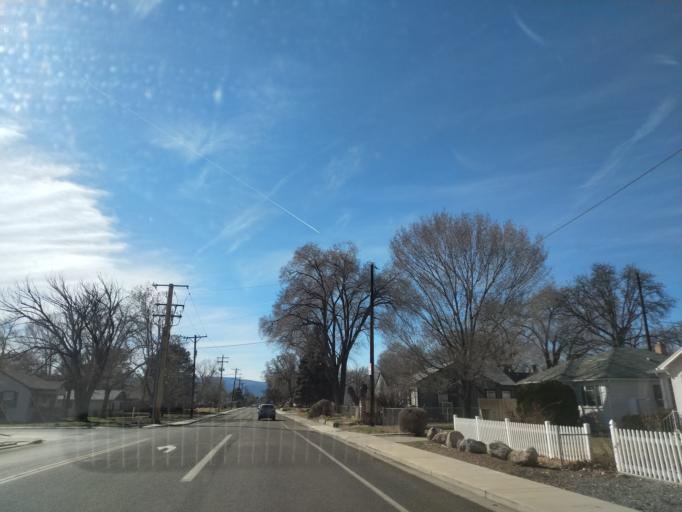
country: US
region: Colorado
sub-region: Mesa County
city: Grand Junction
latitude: 39.0846
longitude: -108.5566
